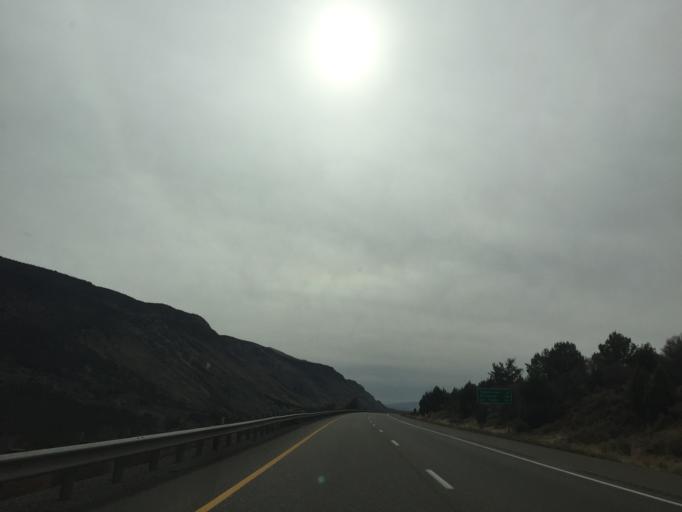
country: US
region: Utah
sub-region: Washington County
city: Toquerville
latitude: 37.3948
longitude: -113.2424
